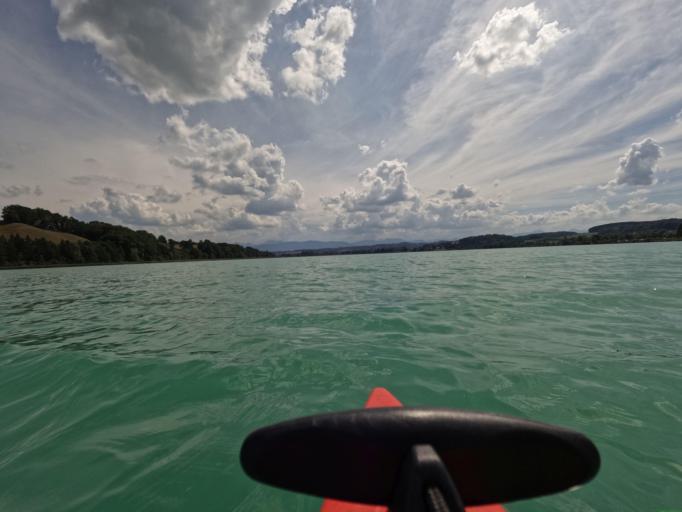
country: DE
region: Bavaria
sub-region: Upper Bavaria
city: Taching am See
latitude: 47.9698
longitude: 12.7423
